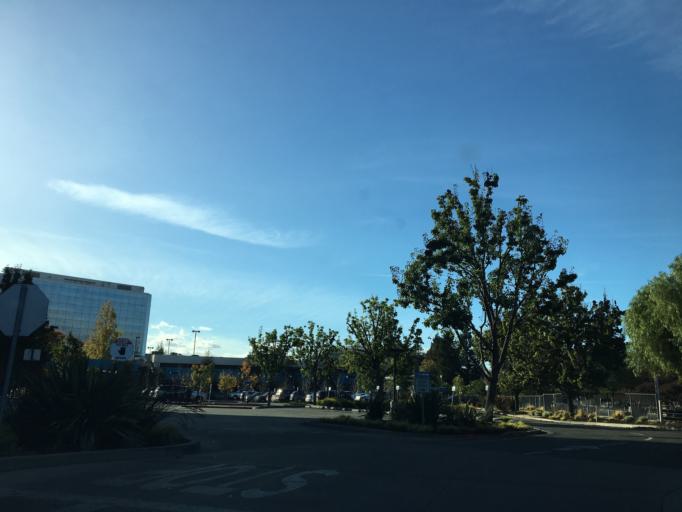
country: US
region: California
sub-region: Santa Clara County
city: Santa Clara
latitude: 37.3884
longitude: -121.9635
